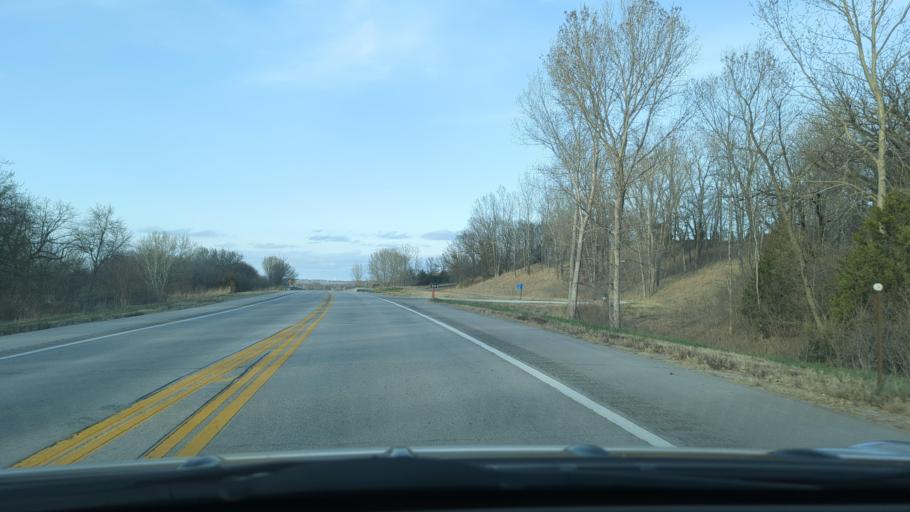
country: US
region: Nebraska
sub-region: Saunders County
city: Ashland
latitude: 41.0475
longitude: -96.3435
